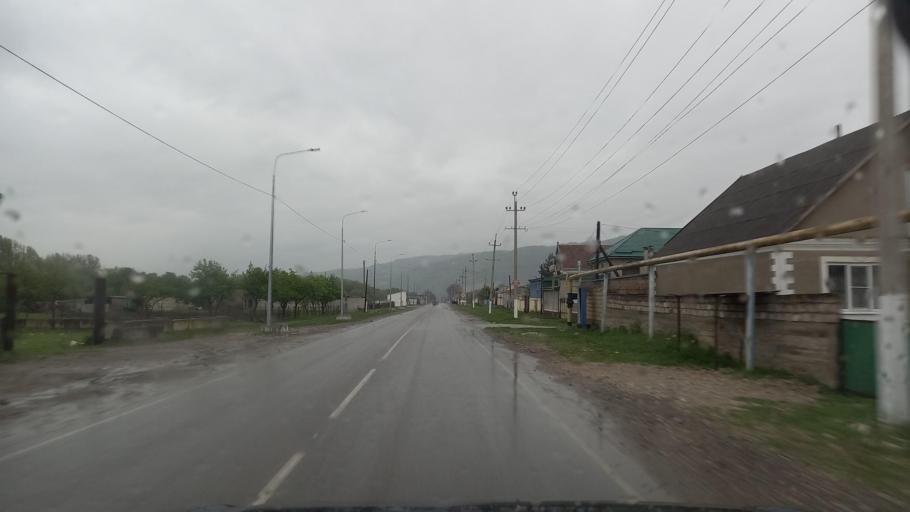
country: RU
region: Kabardino-Balkariya
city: Zhankhoteko
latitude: 43.5888
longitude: 43.2091
